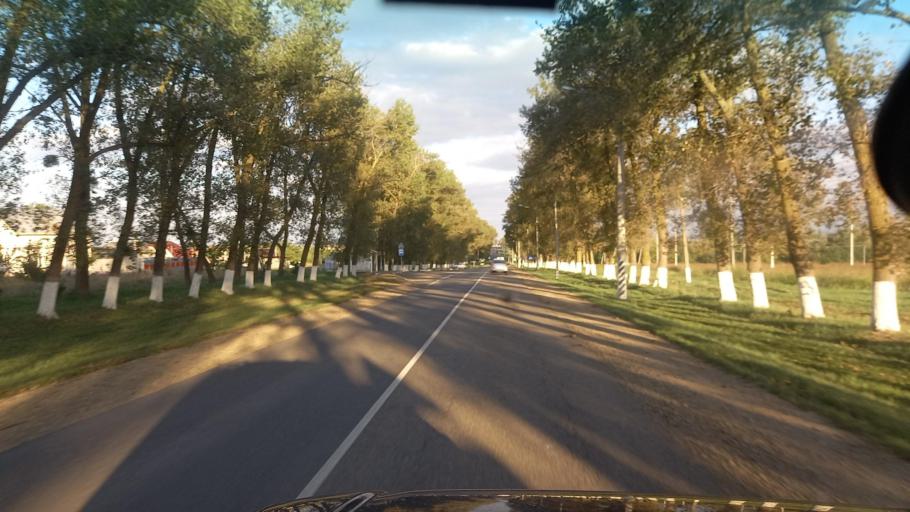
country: RU
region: Krasnodarskiy
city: Krymsk
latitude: 44.9396
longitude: 37.9341
